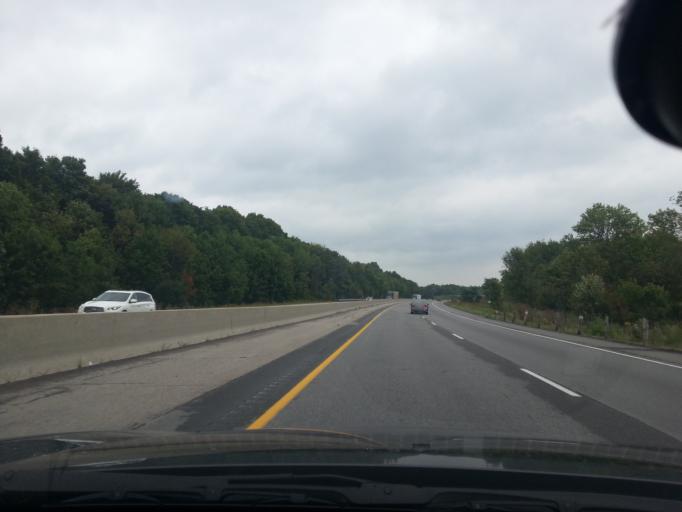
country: CA
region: Ontario
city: Brockville
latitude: 44.5496
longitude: -75.7654
